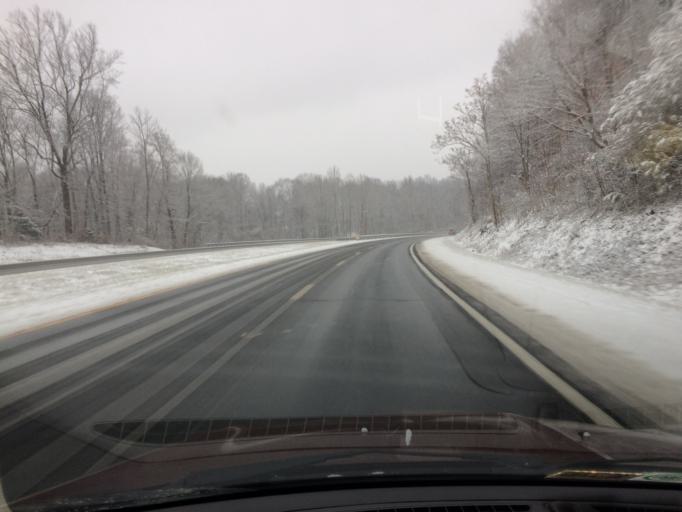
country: US
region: Virginia
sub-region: Amherst County
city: Amherst
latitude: 37.5705
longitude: -79.0533
